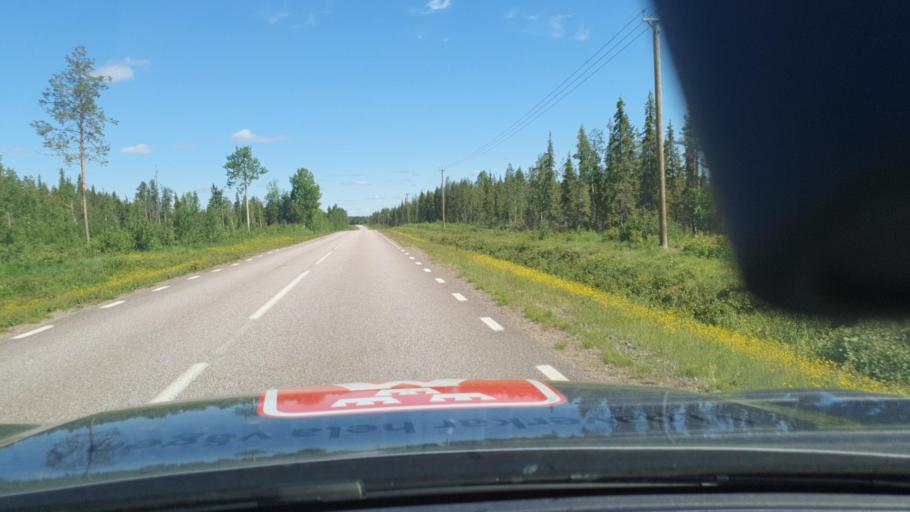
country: SE
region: Norrbotten
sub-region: Overkalix Kommun
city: OEverkalix
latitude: 66.8806
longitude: 22.7643
